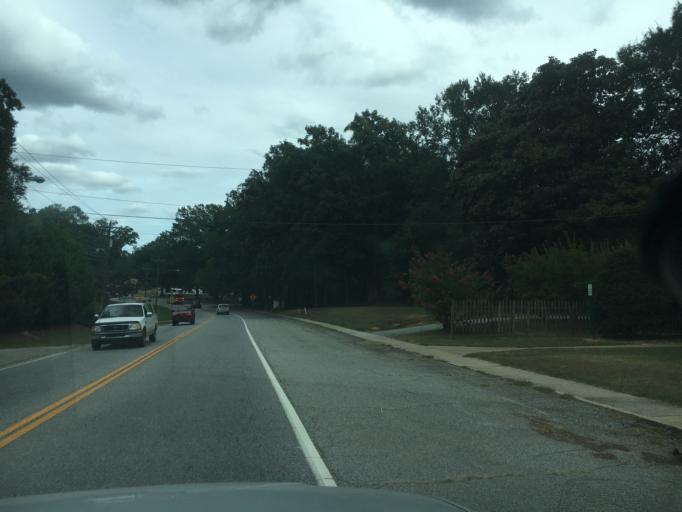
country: US
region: South Carolina
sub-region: Laurens County
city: Laurens
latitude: 34.4934
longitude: -82.0347
